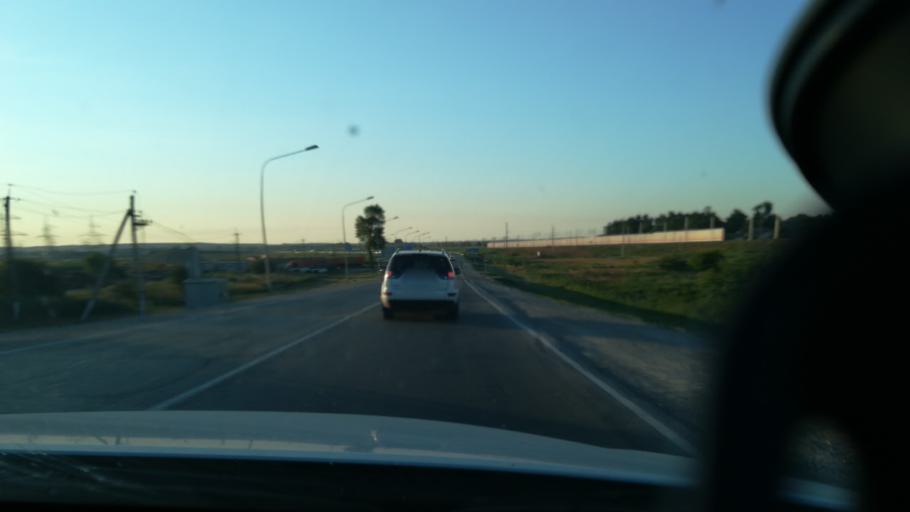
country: RU
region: Krasnodarskiy
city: Dzhiginka
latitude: 45.1288
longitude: 37.3245
